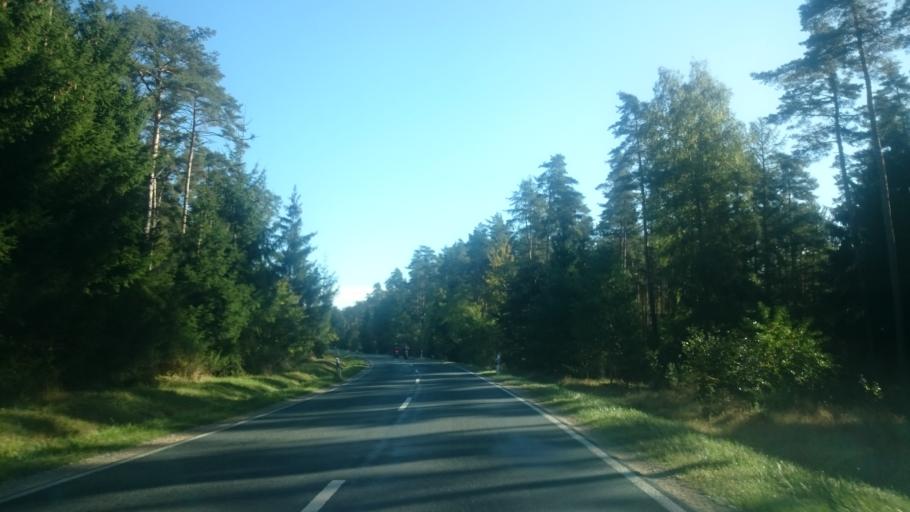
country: DE
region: Bavaria
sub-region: Regierungsbezirk Mittelfranken
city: Rottenbach
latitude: 49.1314
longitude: 11.0428
